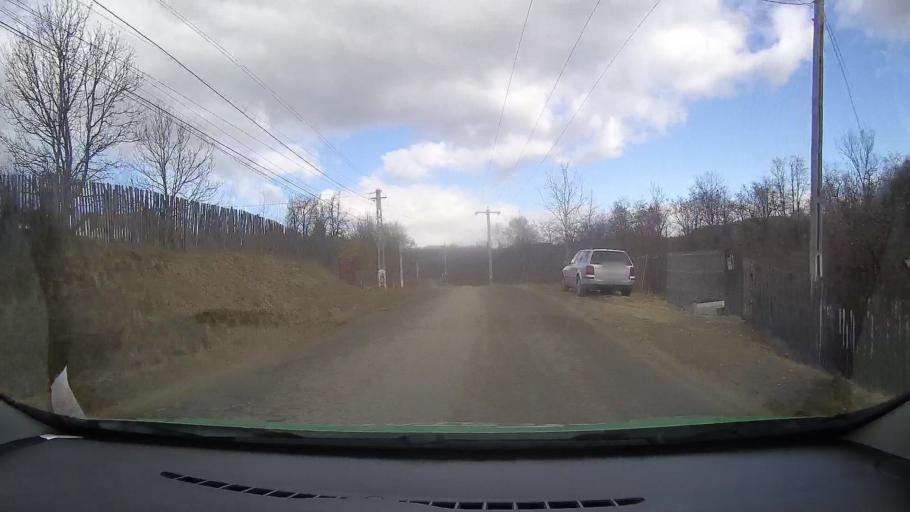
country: RO
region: Dambovita
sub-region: Comuna Buciumeni
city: Buciumeni
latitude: 45.1319
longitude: 25.4678
